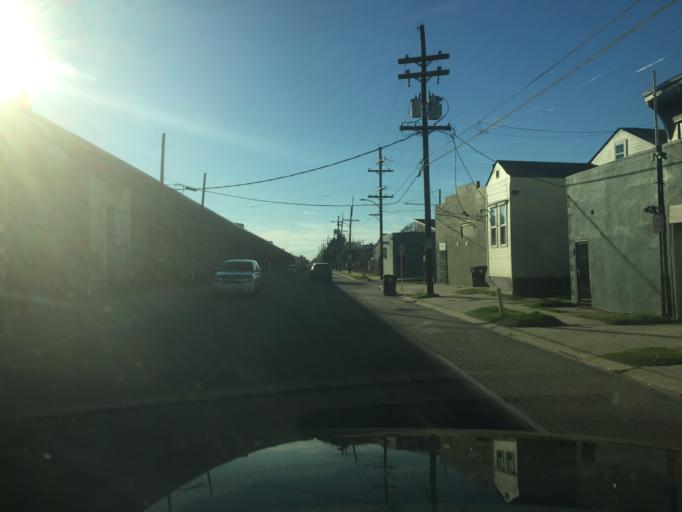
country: US
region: Louisiana
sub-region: Jefferson Parish
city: Harvey
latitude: 29.9182
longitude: -90.0892
